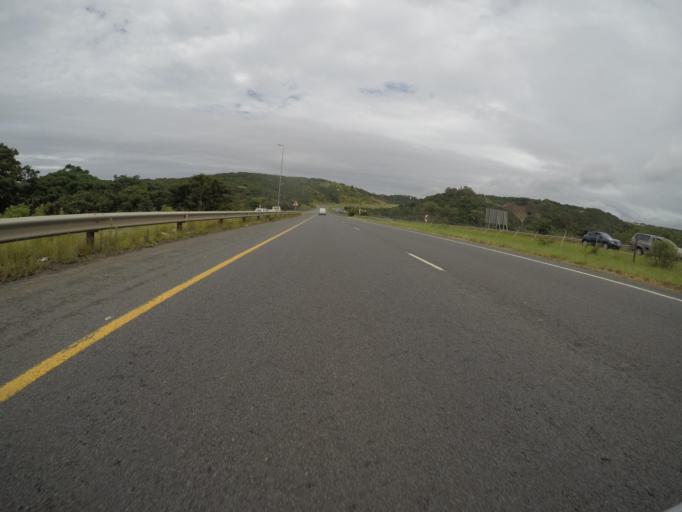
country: ZA
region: Eastern Cape
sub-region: Buffalo City Metropolitan Municipality
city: East London
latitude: -32.9645
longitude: 27.9193
